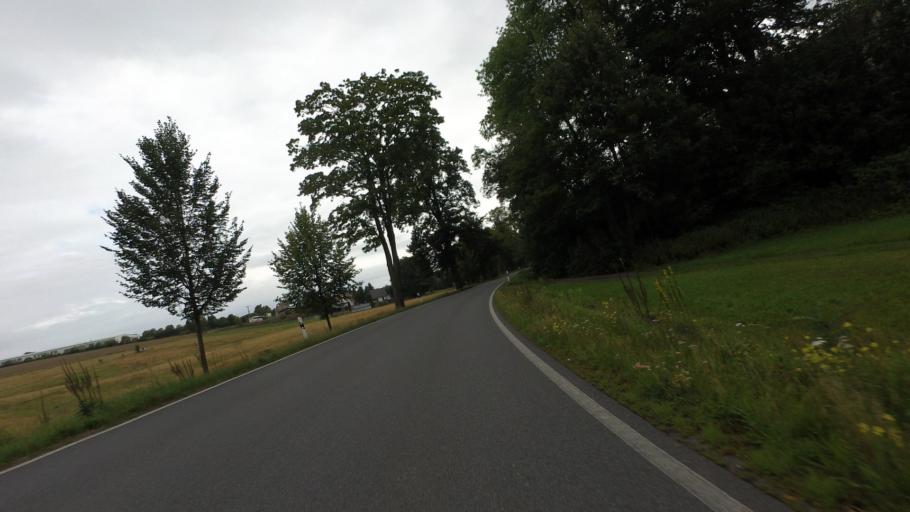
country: DE
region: Saxony
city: Berthelsdorf
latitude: 51.0415
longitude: 14.2189
